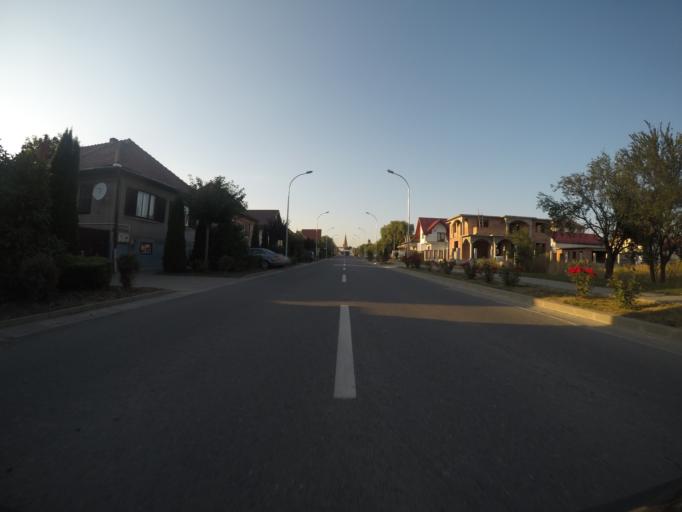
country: RO
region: Sibiu
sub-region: Comuna Selimbar
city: Selimbar
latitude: 45.7636
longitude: 24.1967
